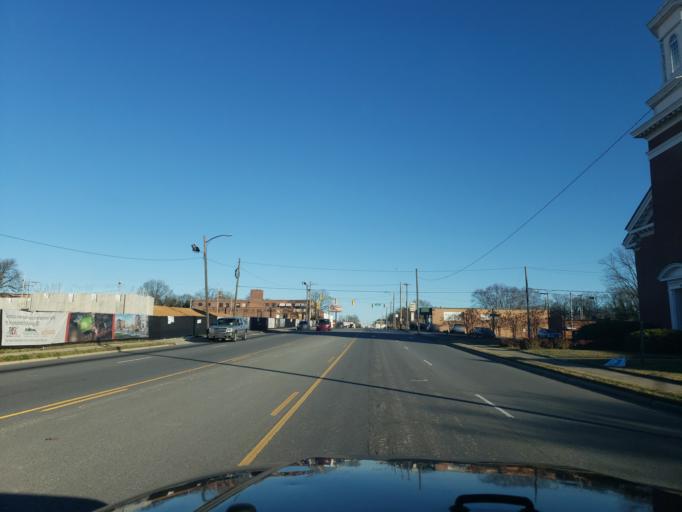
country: US
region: North Carolina
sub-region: Gaston County
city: Gastonia
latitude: 35.2623
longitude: -81.1948
